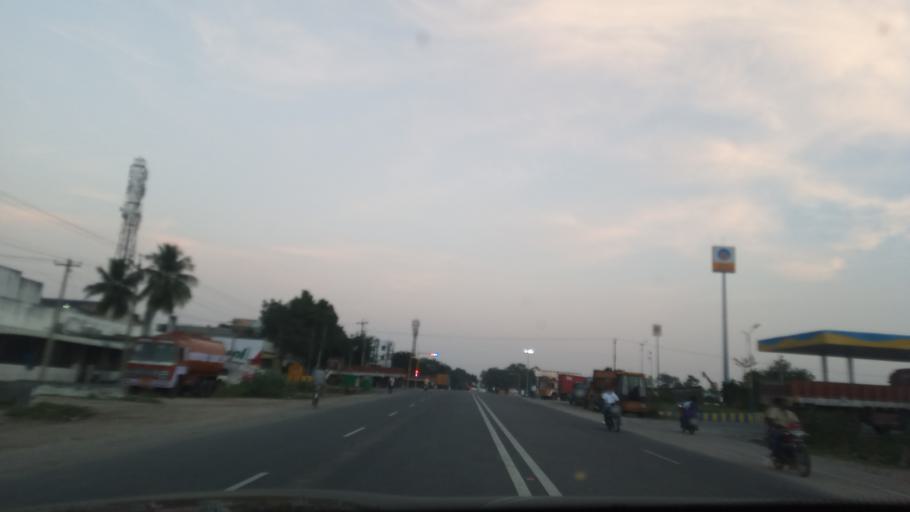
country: IN
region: Tamil Nadu
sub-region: Vellore
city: Walajapet
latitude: 12.9275
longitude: 79.3471
